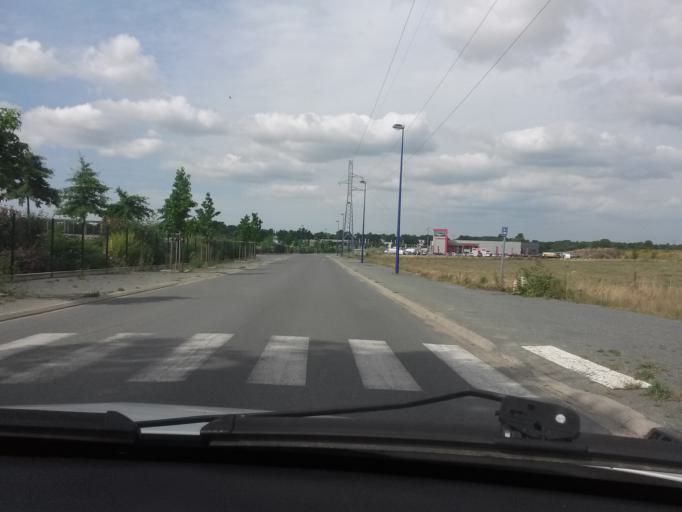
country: FR
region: Pays de la Loire
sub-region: Departement de la Vendee
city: Mouilleron-le-Captif
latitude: 46.7175
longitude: -1.4252
